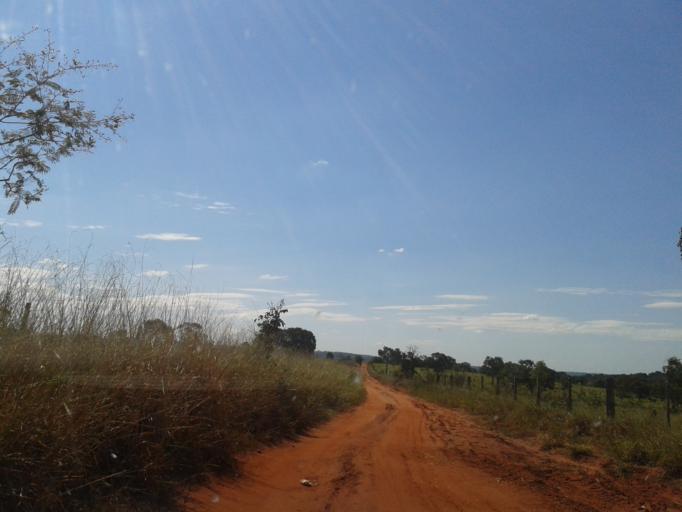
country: BR
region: Minas Gerais
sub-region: Campina Verde
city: Campina Verde
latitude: -19.3977
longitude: -49.7538
